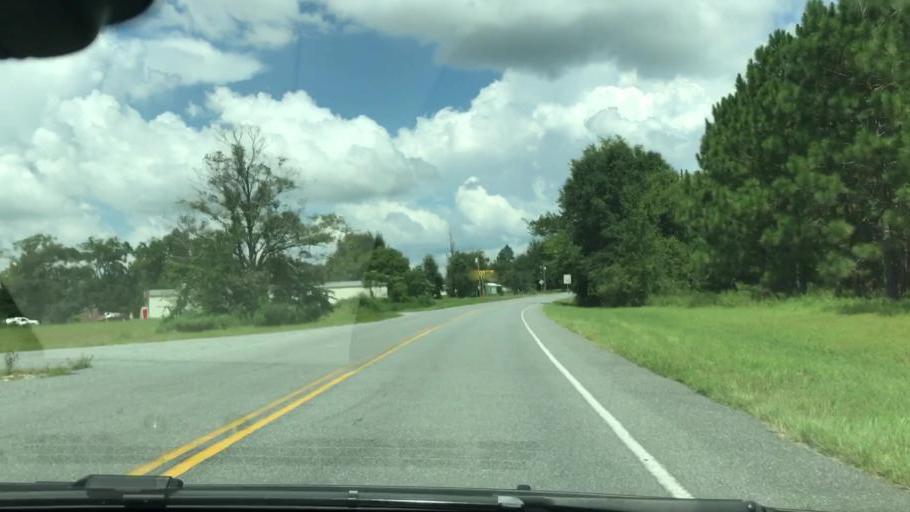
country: US
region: Florida
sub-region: Jackson County
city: Malone
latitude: 30.8809
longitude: -85.1606
